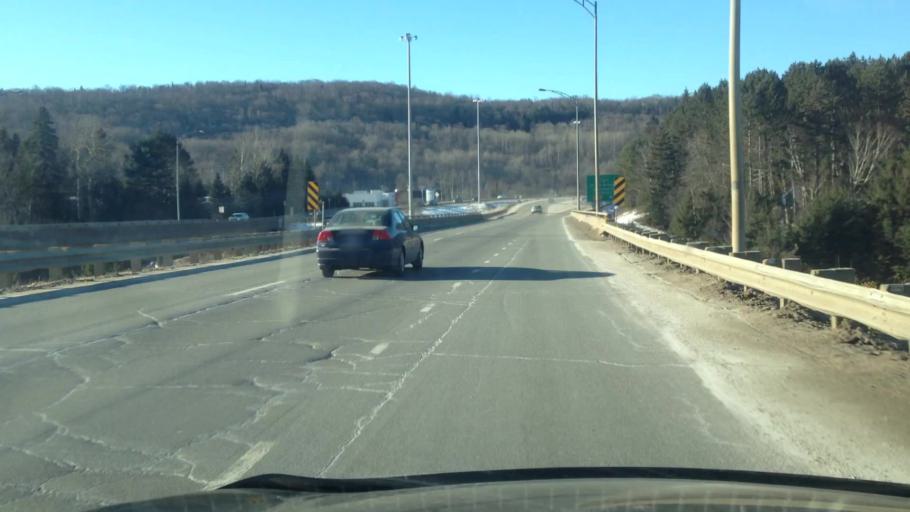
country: CA
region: Quebec
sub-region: Laurentides
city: Mont-Tremblant
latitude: 46.1136
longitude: -74.6006
